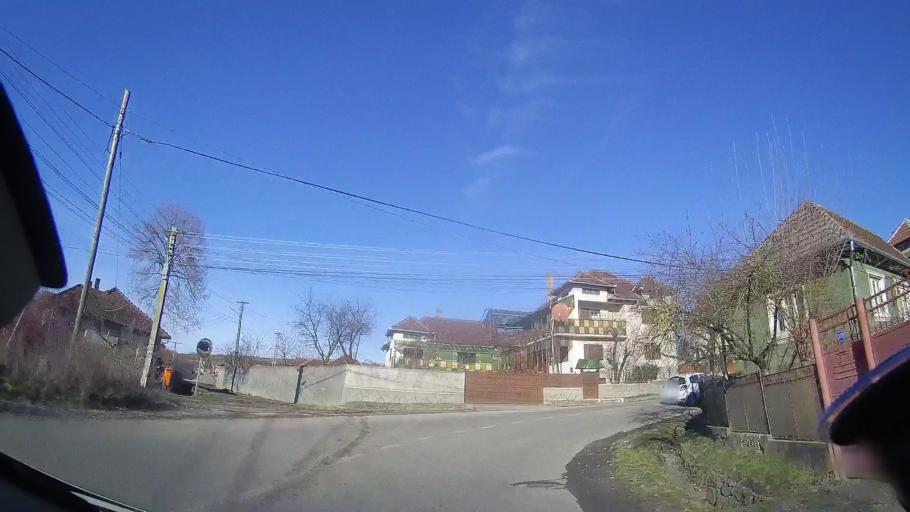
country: RO
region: Bihor
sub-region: Comuna Bratca
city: Beznea
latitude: 46.9546
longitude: 22.6103
